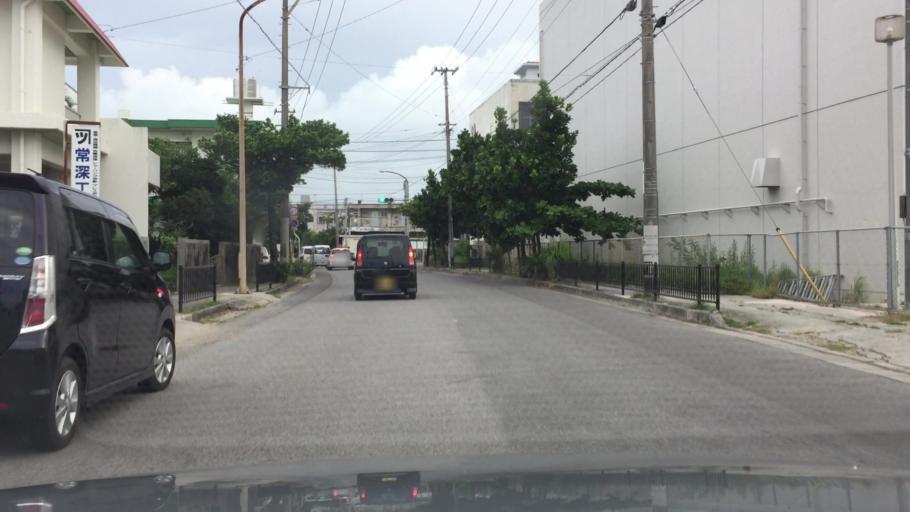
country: JP
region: Okinawa
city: Ishigaki
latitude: 24.3490
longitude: 124.1583
